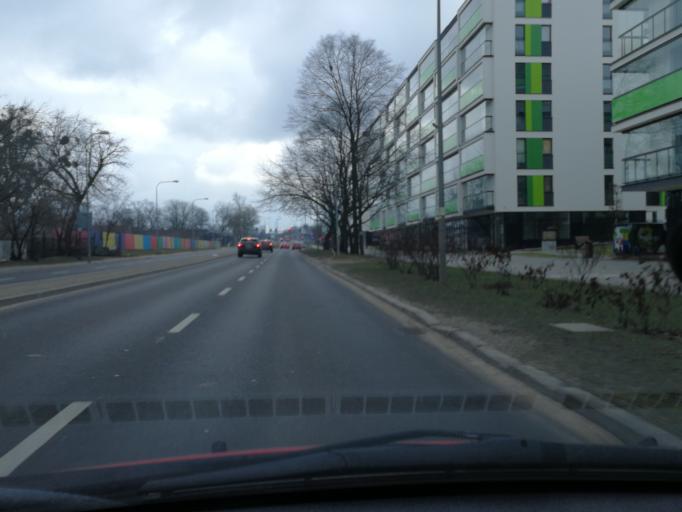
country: PL
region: Masovian Voivodeship
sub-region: Warszawa
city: Zoliborz
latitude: 52.2578
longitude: 20.9644
